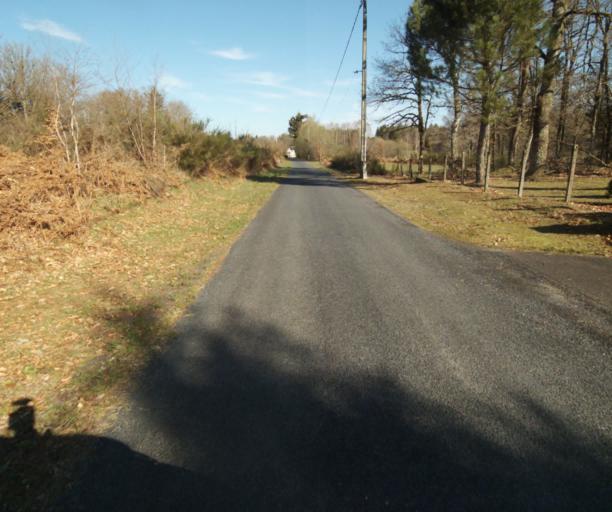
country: FR
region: Limousin
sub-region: Departement de la Correze
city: Correze
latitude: 45.2699
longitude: 1.9260
